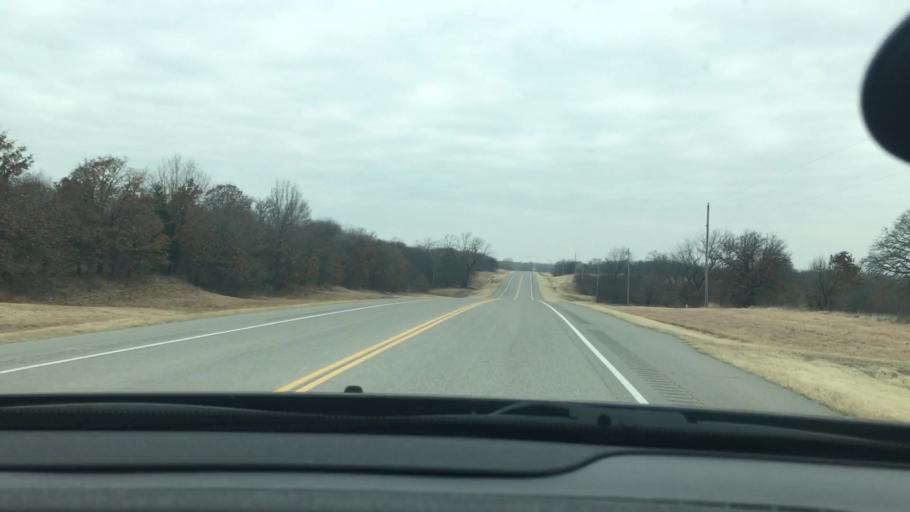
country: US
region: Oklahoma
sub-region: Carter County
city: Healdton
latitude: 34.4925
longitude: -97.4277
